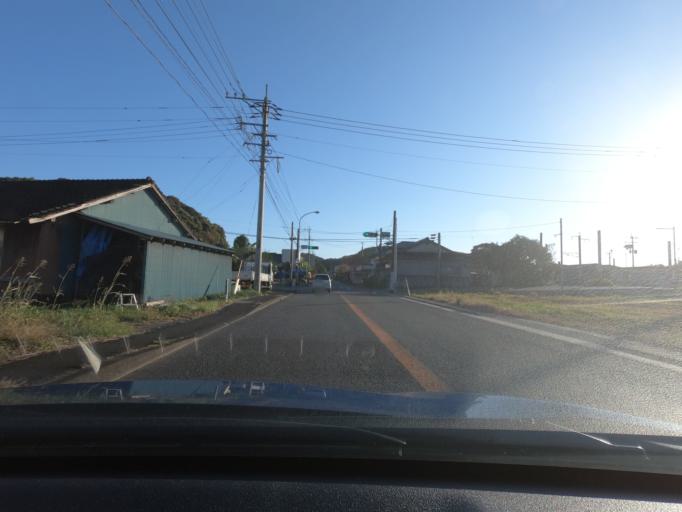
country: JP
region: Kagoshima
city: Satsumasendai
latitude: 31.8675
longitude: 130.2249
